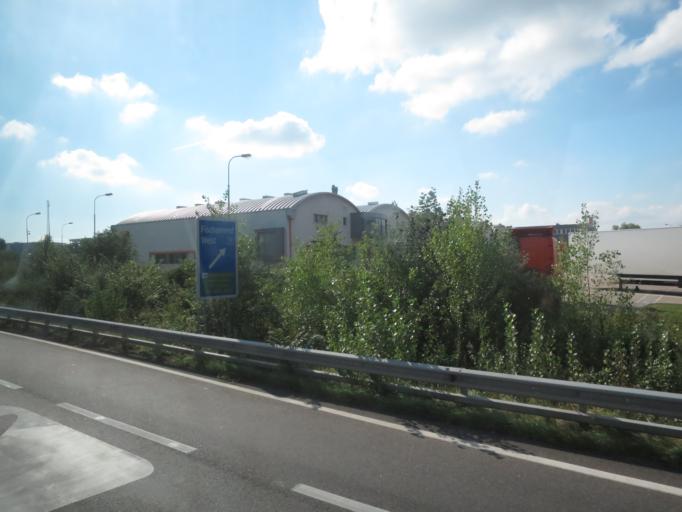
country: AT
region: Lower Austria
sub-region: Politischer Bezirk Wien-Umgebung
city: Rauchenwarth
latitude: 48.1284
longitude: 16.5525
